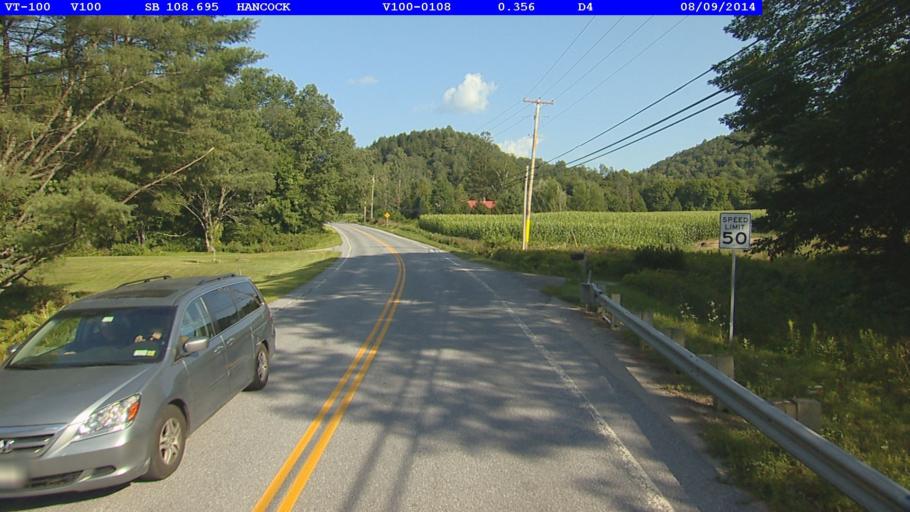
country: US
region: Vermont
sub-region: Orange County
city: Randolph
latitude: 43.9145
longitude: -72.8392
